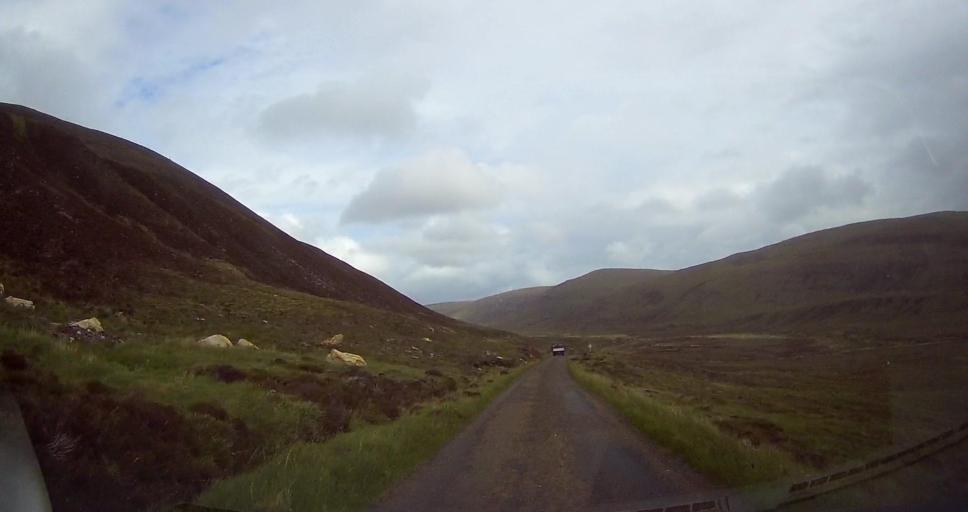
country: GB
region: Scotland
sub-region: Orkney Islands
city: Stromness
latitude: 58.8821
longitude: -3.3601
